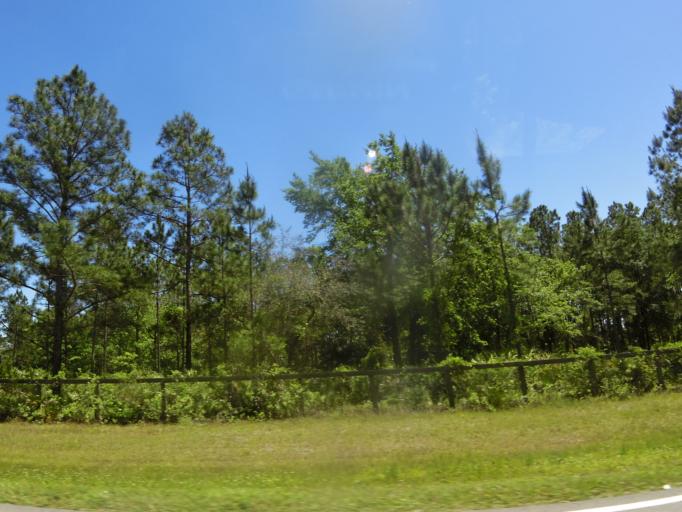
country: US
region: Florida
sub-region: Saint Johns County
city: Fruit Cove
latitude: 30.0454
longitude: -81.5778
